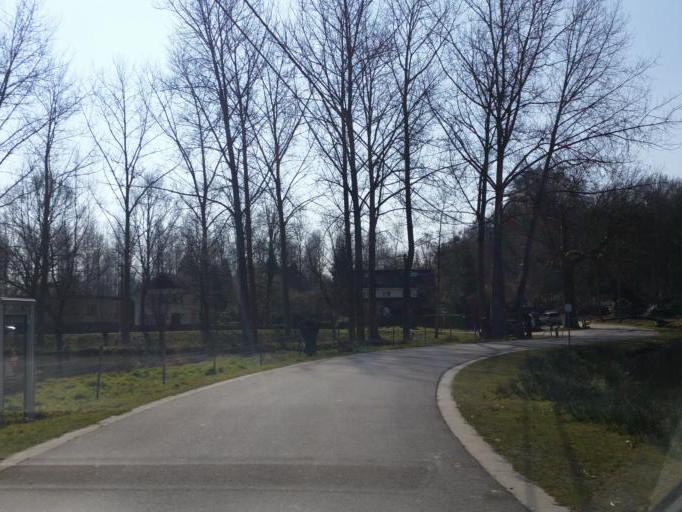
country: BE
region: Flanders
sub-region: Provincie Oost-Vlaanderen
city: Kruibeke
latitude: 51.1461
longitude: 4.3045
